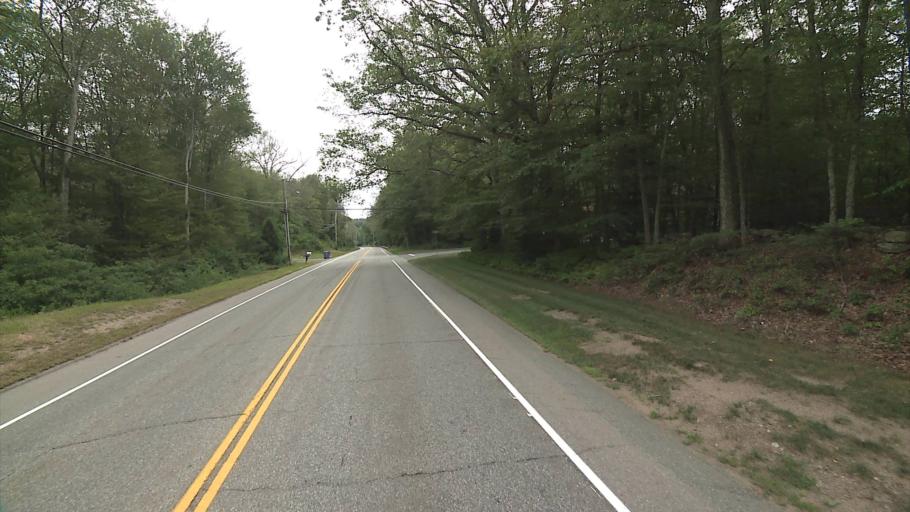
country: US
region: Connecticut
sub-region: Hartford County
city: Terramuggus
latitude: 41.6898
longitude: -72.4312
